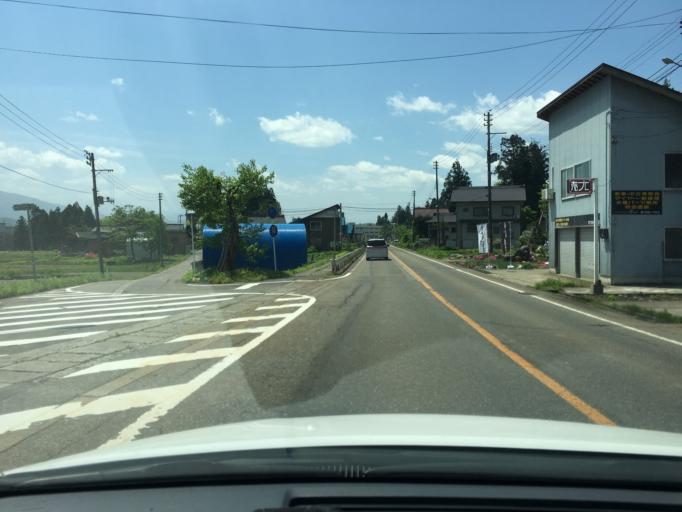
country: JP
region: Niigata
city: Ojiya
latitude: 37.2644
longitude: 138.9740
